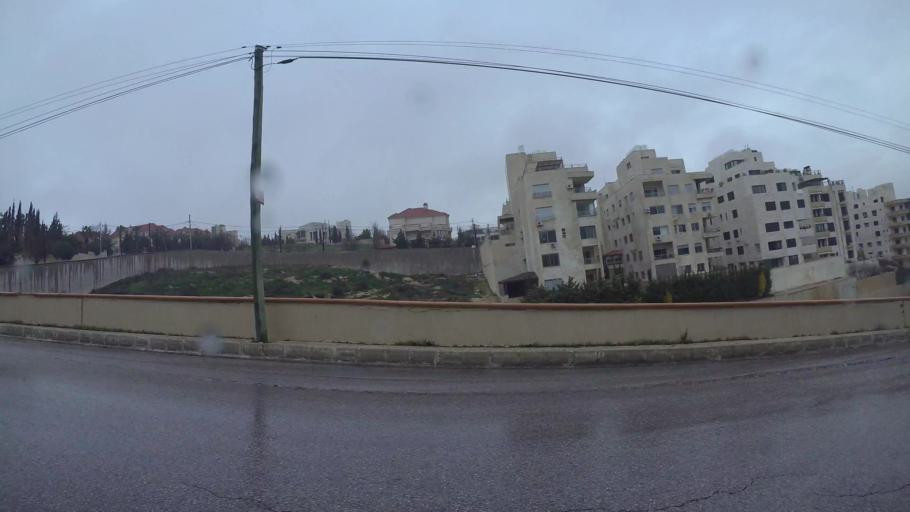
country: JO
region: Amman
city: Al Jubayhah
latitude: 32.0071
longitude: 35.8274
